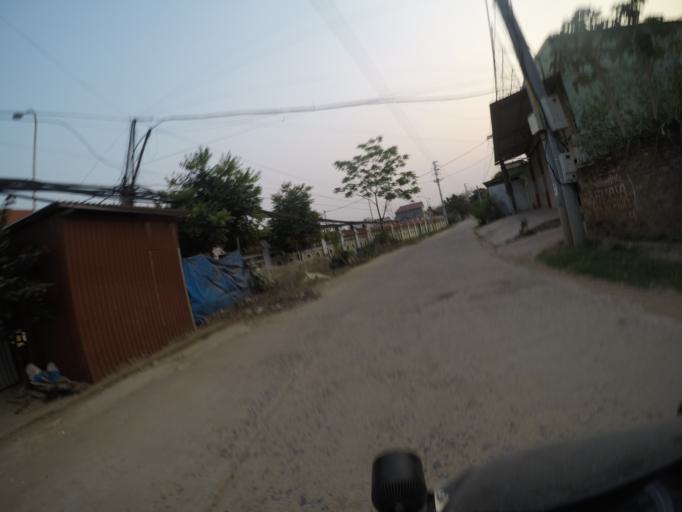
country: VN
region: Vinh Phuc
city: Trai Ngau
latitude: 21.4597
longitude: 105.5694
